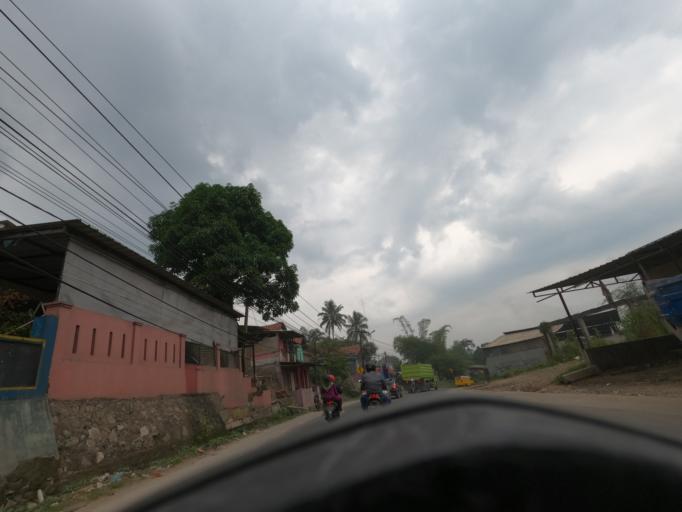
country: ID
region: West Java
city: Padalarang
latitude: -6.8326
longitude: 107.4355
